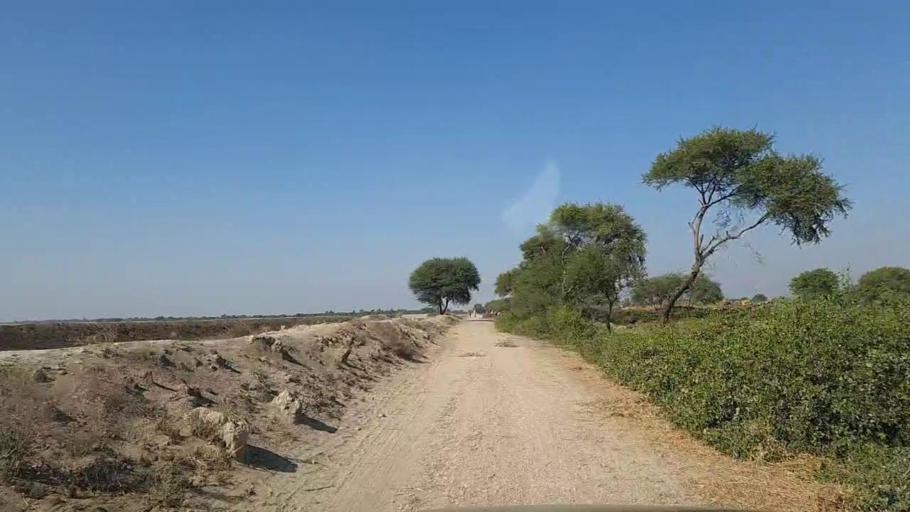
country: PK
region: Sindh
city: Mirpur Batoro
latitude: 24.7211
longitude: 68.2343
